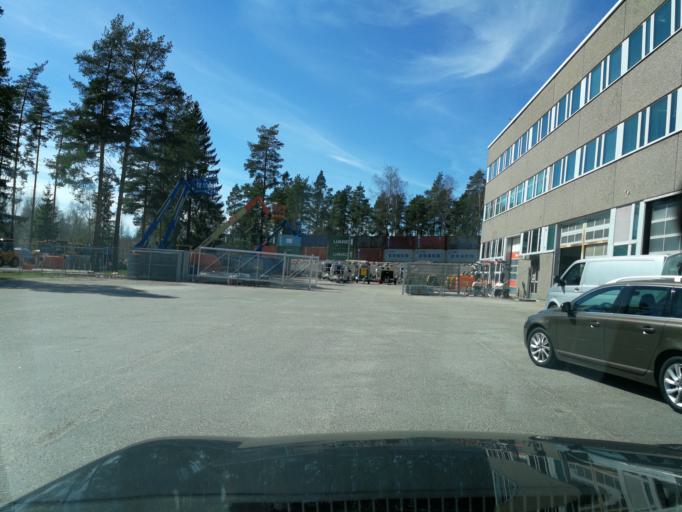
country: FI
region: Uusimaa
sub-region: Helsinki
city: Koukkuniemi
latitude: 60.1557
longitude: 24.7096
